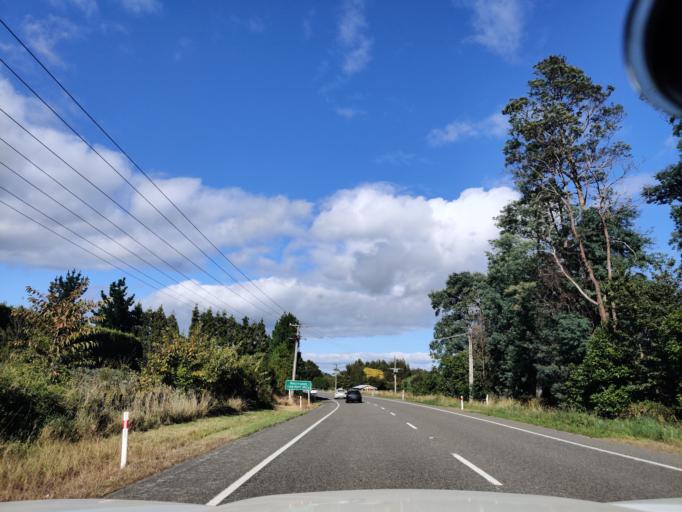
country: NZ
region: Manawatu-Wanganui
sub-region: Horowhenua District
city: Levin
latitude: -40.6511
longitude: 175.2852
